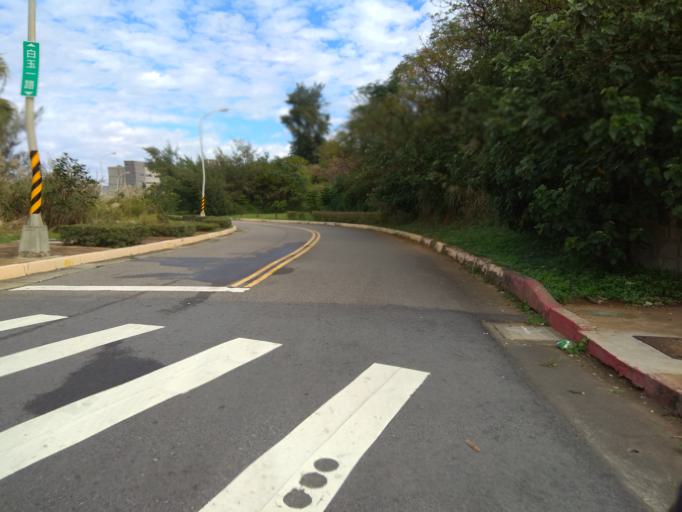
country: TW
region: Taiwan
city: Taoyuan City
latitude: 25.0447
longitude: 121.0865
